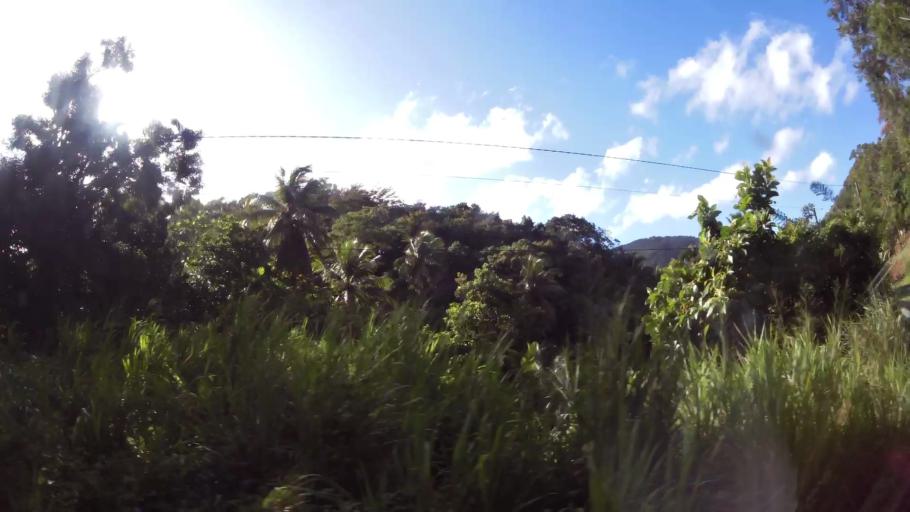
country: DM
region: Saint John
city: Portsmouth
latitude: 15.5760
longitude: -61.4290
